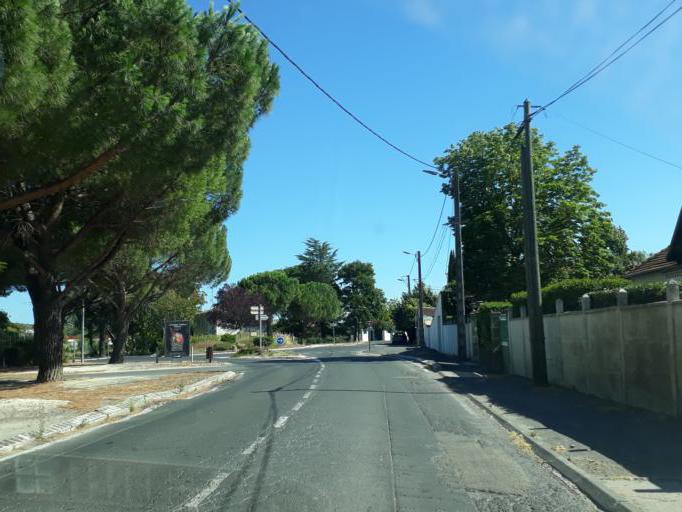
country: FR
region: Languedoc-Roussillon
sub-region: Departement de l'Herault
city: Pezenas
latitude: 43.4540
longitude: 3.4268
